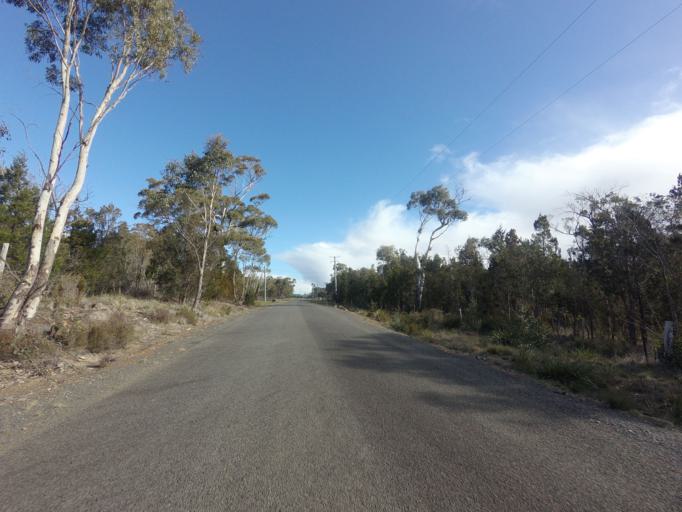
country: AU
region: Tasmania
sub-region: Sorell
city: Sorell
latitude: -42.3038
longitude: 147.9923
